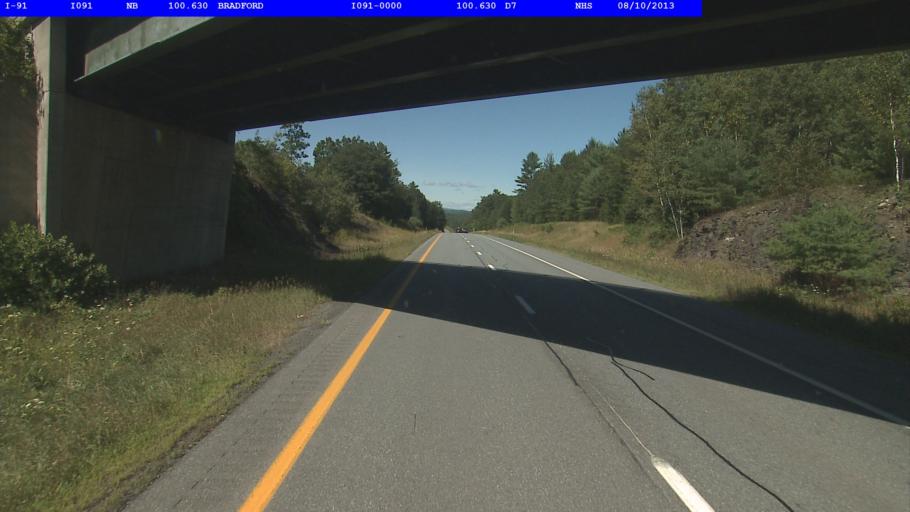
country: US
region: New Hampshire
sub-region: Grafton County
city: Haverhill
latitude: 44.0236
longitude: -72.1166
